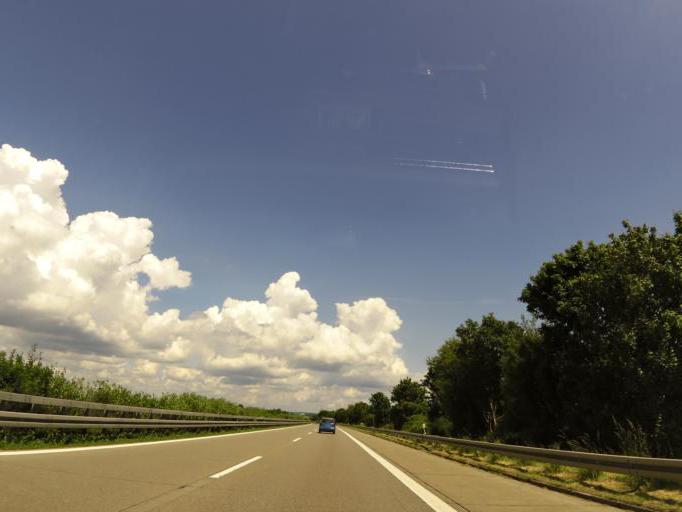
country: DE
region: Baden-Wuerttemberg
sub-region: Regierungsbezirk Stuttgart
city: Herbrechtingen
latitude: 48.5918
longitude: 10.1859
